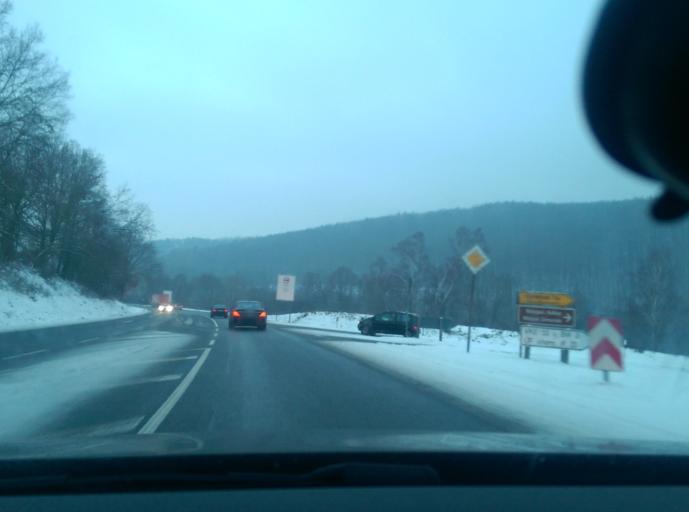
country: DE
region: Hesse
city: Waldkappel
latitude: 51.1632
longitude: 9.8520
